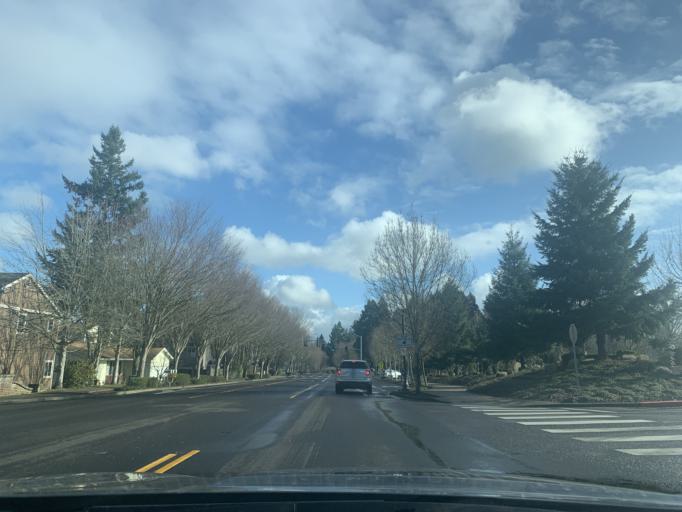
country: US
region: Oregon
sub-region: Washington County
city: Sherwood
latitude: 45.3587
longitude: -122.8519
